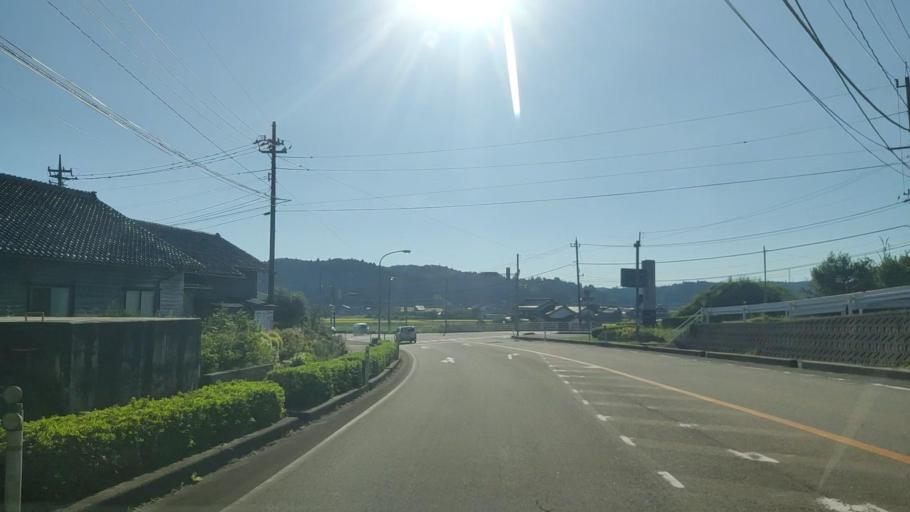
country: JP
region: Ishikawa
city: Nanao
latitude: 37.1172
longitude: 136.8589
